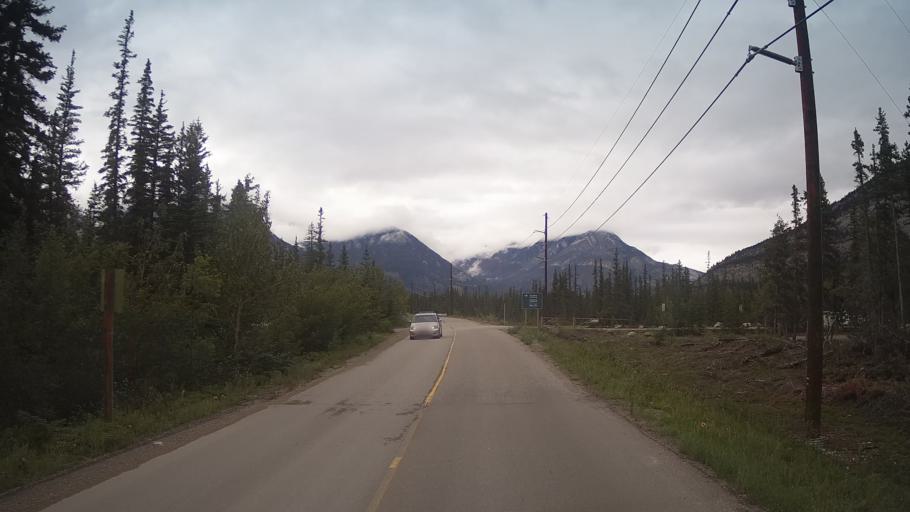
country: CA
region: Alberta
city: Jasper Park Lodge
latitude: 53.0139
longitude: -118.0866
